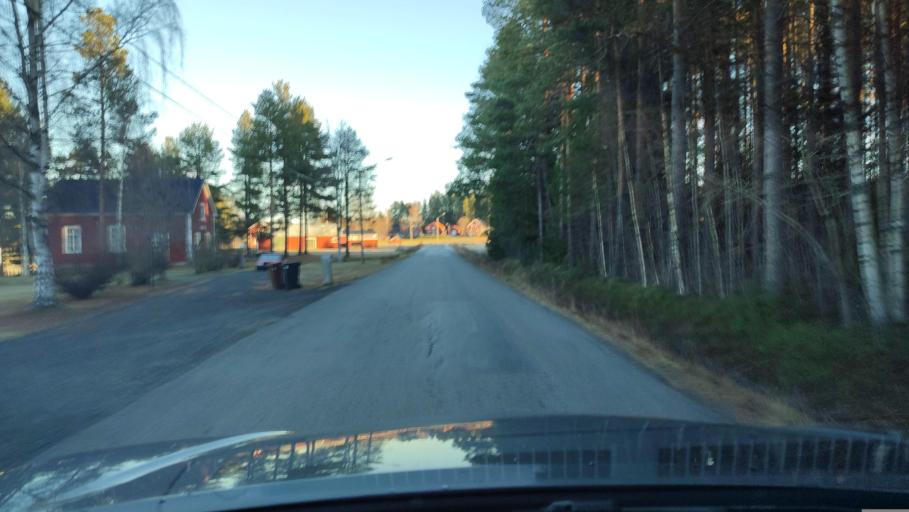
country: SE
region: Vaesterbotten
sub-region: Skelleftea Kommun
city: Soedra Bergsbyn
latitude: 64.6313
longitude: 21.0599
